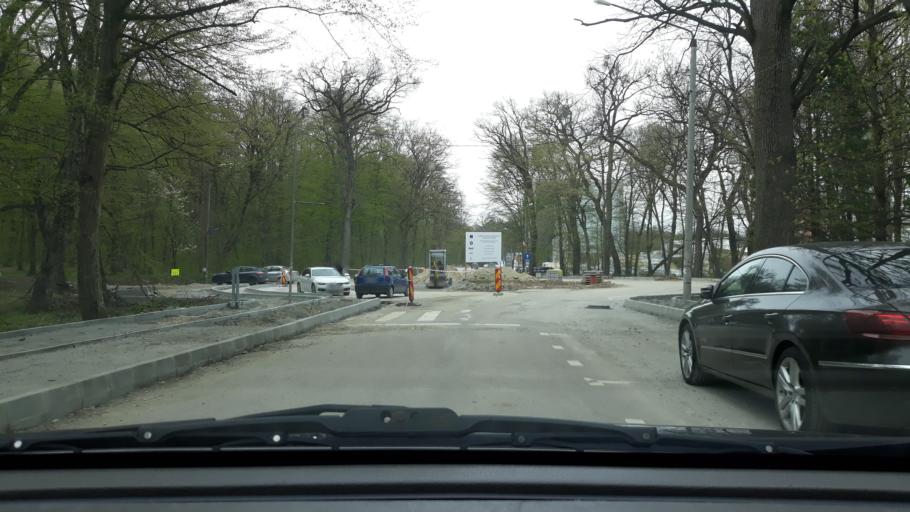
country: RO
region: Bihor
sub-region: Comuna Sanmartin
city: Sanmartin
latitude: 46.9871
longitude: 21.9764
